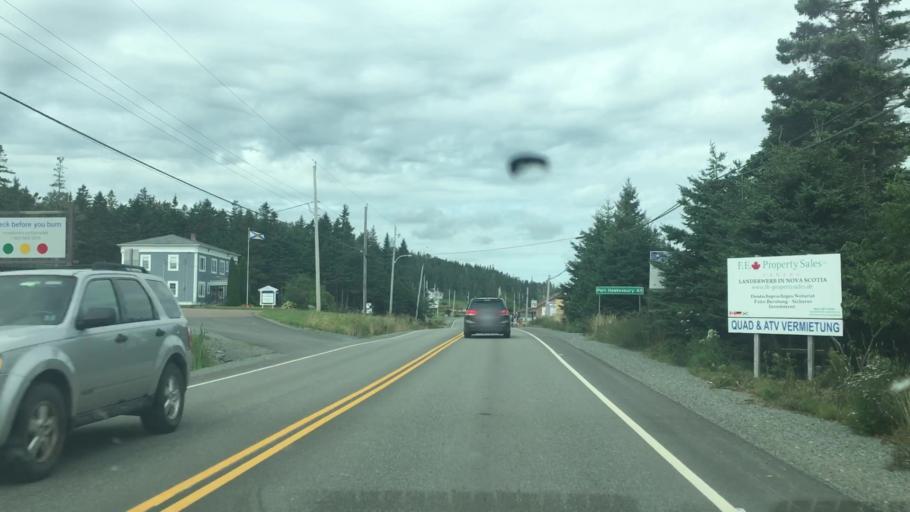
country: CA
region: Nova Scotia
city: Princeville
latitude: 45.6523
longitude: -60.8583
